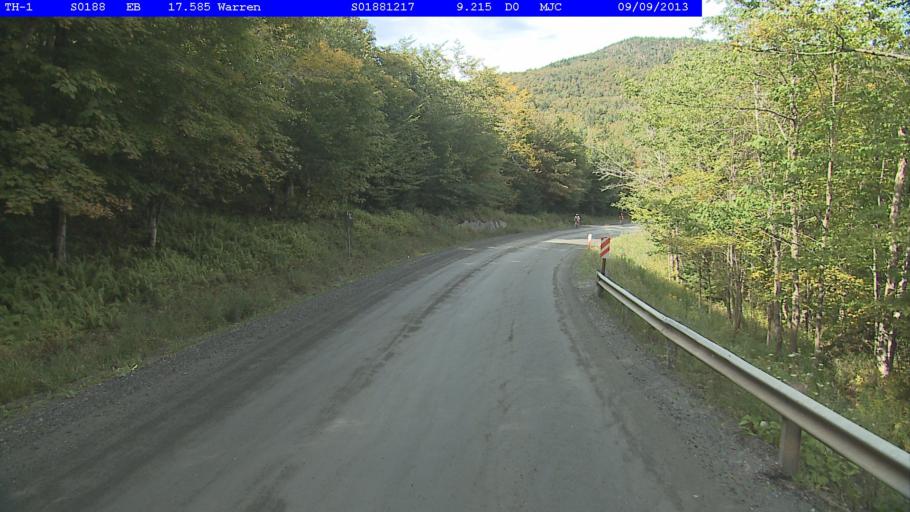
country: US
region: Vermont
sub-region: Washington County
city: Northfield
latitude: 44.1125
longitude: -72.7837
